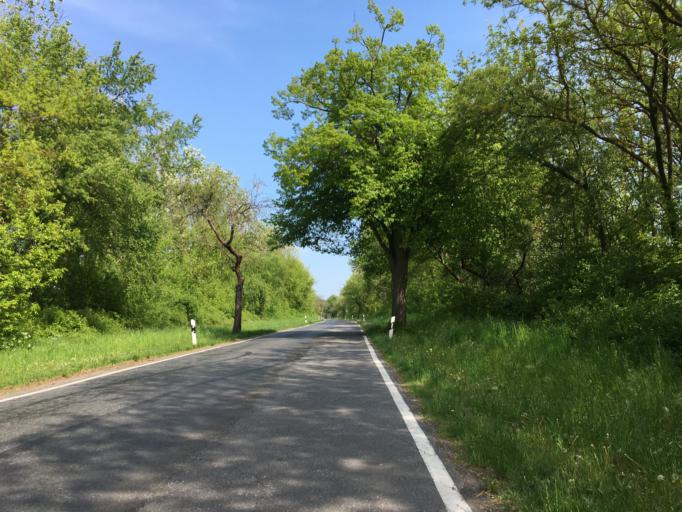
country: DE
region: Brandenburg
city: Werneuchen
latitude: 52.6599
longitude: 13.7311
